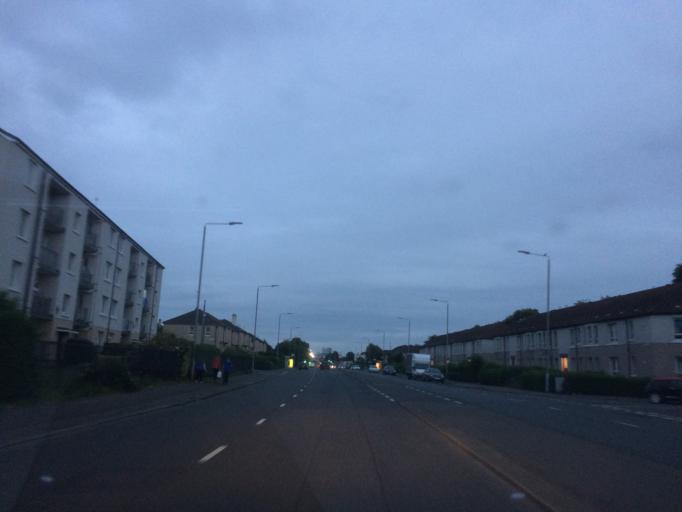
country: GB
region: Scotland
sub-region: Renfrewshire
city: Renfrew
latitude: 55.8561
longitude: -4.3362
